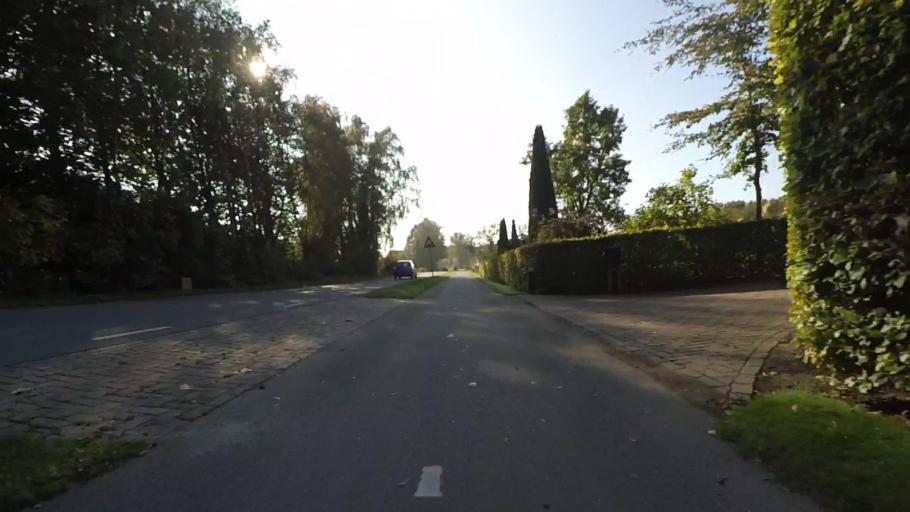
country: NL
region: Gelderland
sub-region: Gemeente Putten
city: Putten
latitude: 52.2735
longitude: 5.6036
